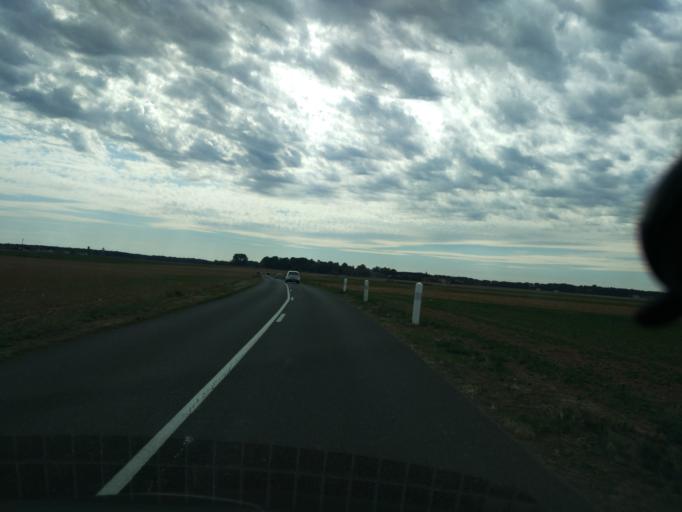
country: FR
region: Ile-de-France
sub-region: Departement de l'Essonne
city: Gometz-la-Ville
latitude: 48.6583
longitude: 2.1246
